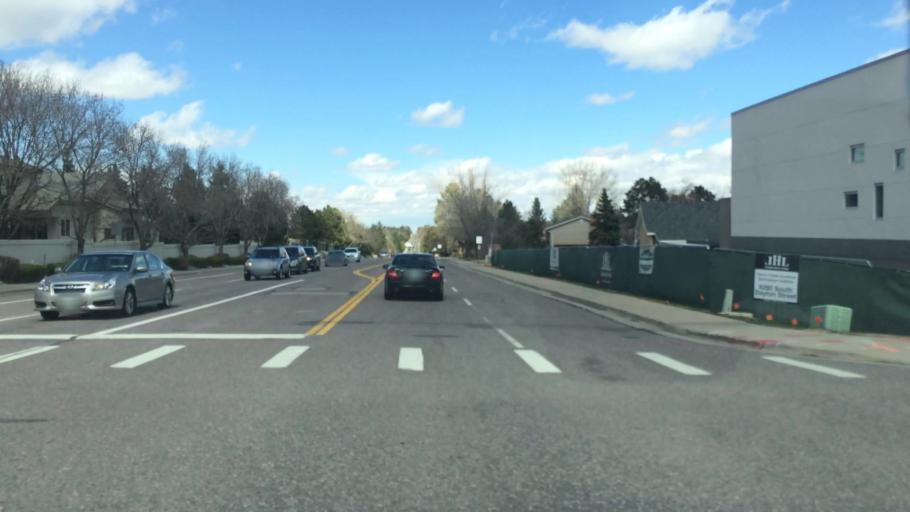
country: US
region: Colorado
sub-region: Arapahoe County
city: Centennial
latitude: 39.6023
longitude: -104.8761
